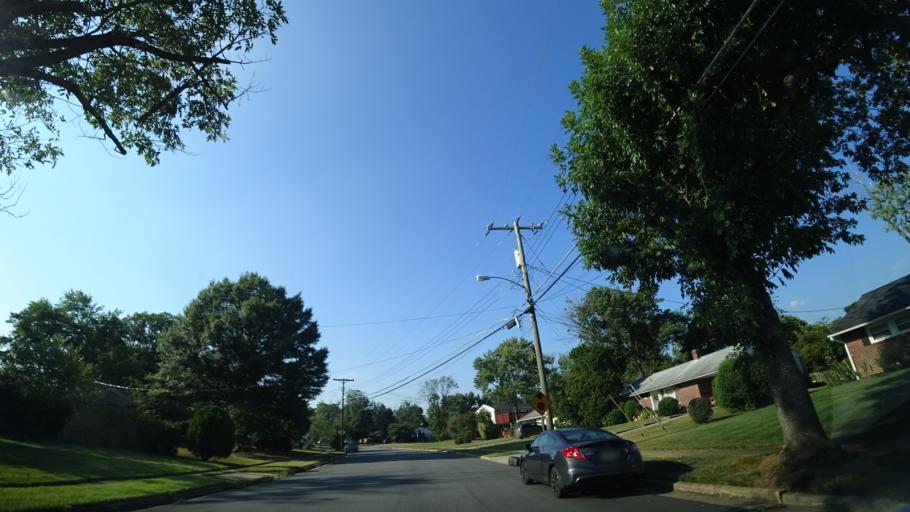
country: US
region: Virginia
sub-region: Fairfax County
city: Springfield
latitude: 38.8080
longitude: -77.1761
